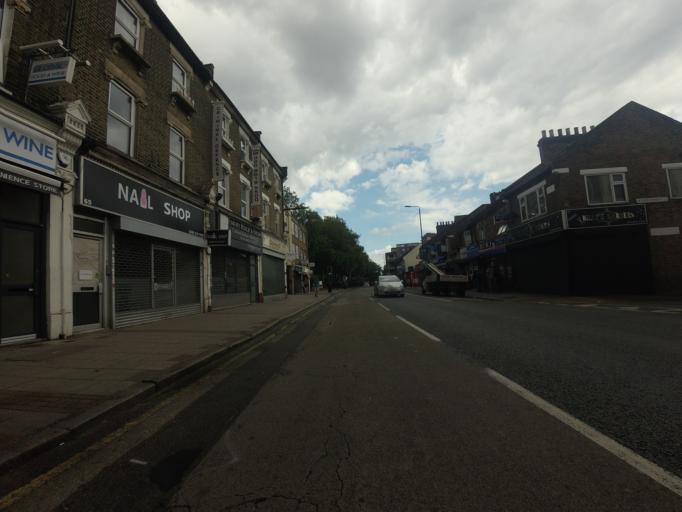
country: GB
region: England
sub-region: Greater London
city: Poplar
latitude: 51.5393
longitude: 0.0044
